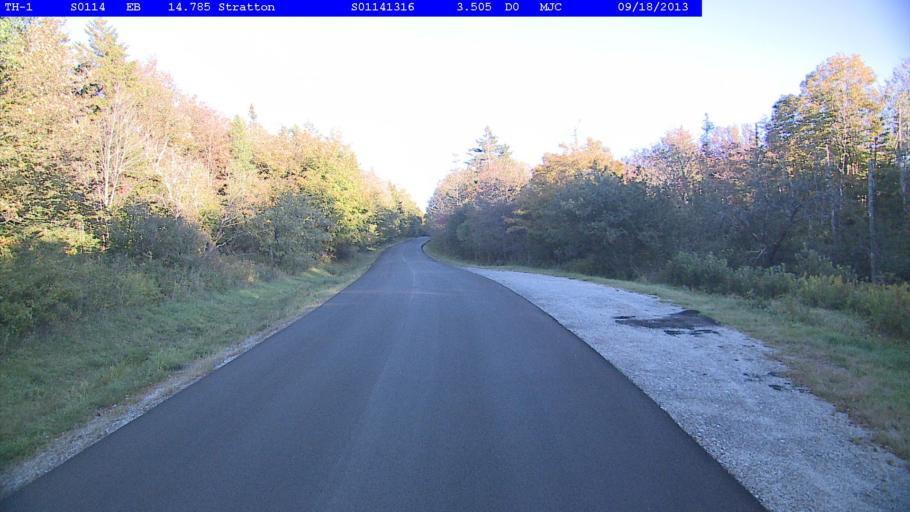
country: US
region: Vermont
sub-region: Bennington County
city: Manchester Center
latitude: 43.0568
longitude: -72.9378
